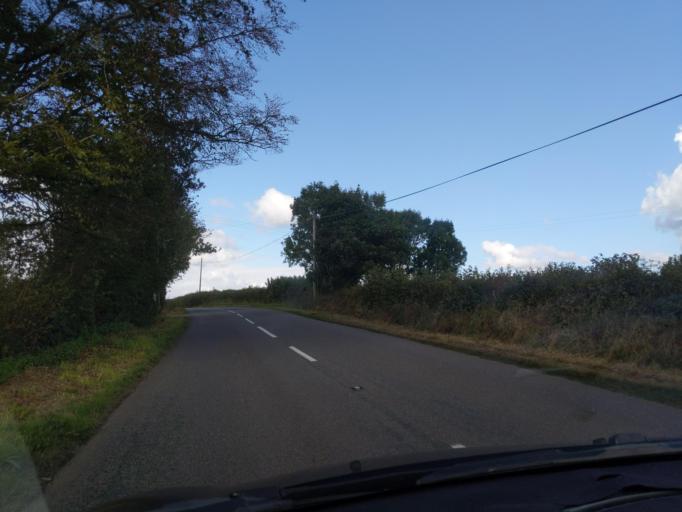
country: GB
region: England
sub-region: Cornwall
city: Werrington
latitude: 50.7054
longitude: -4.3255
